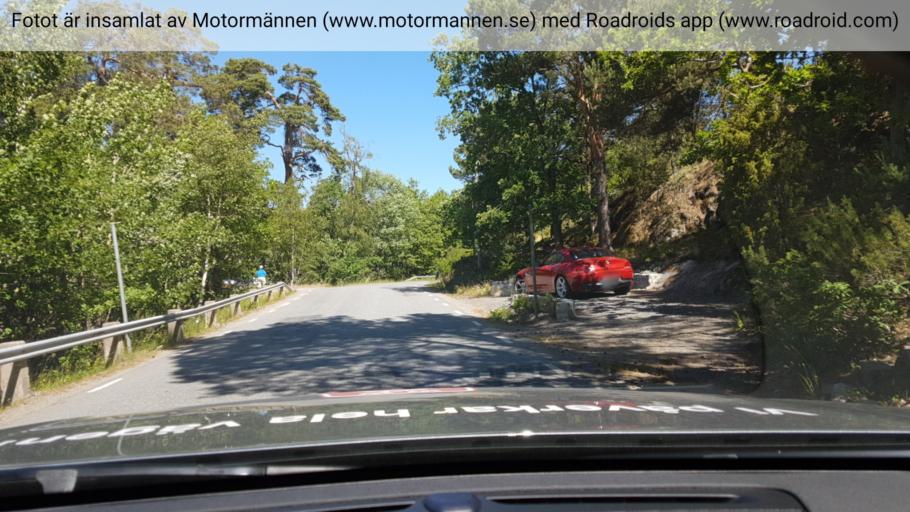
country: SE
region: Stockholm
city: Dalaro
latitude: 59.1558
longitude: 18.4382
